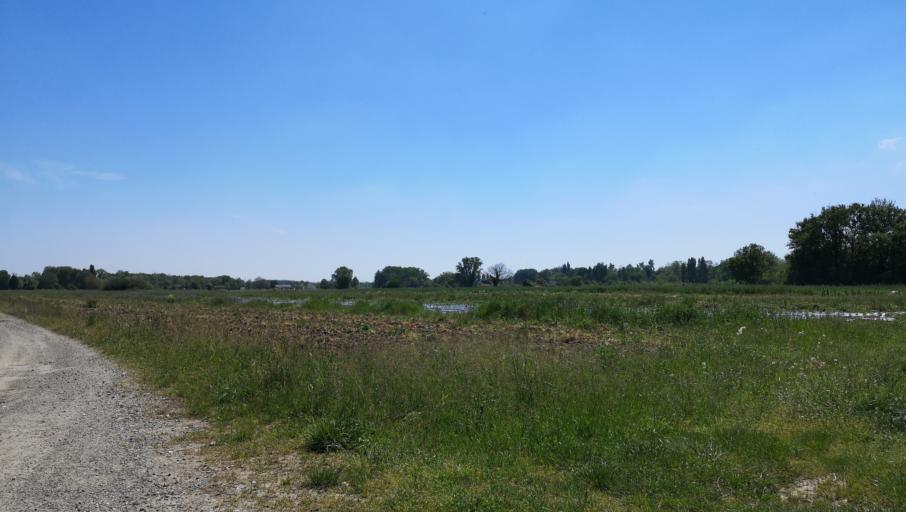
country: FR
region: Midi-Pyrenees
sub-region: Departement de la Haute-Garonne
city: Beauzelle
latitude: 43.6567
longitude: 1.3924
